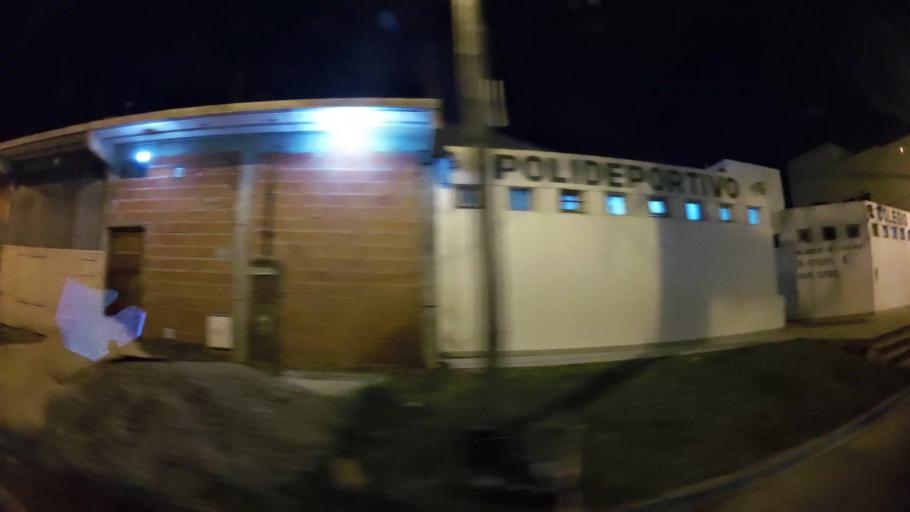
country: AR
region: Buenos Aires
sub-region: Partido de Lanus
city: Lanus
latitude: -34.7242
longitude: -58.3637
